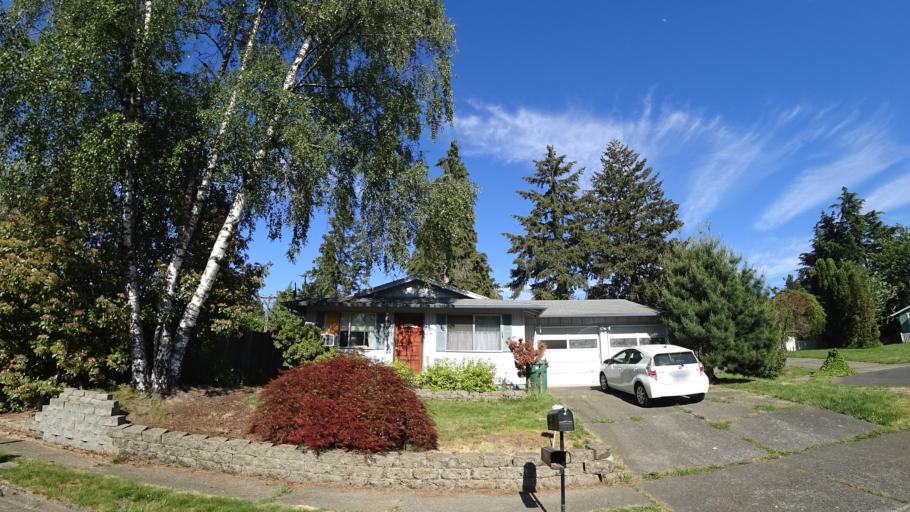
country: US
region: Oregon
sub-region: Washington County
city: Beaverton
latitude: 45.4662
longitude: -122.8069
